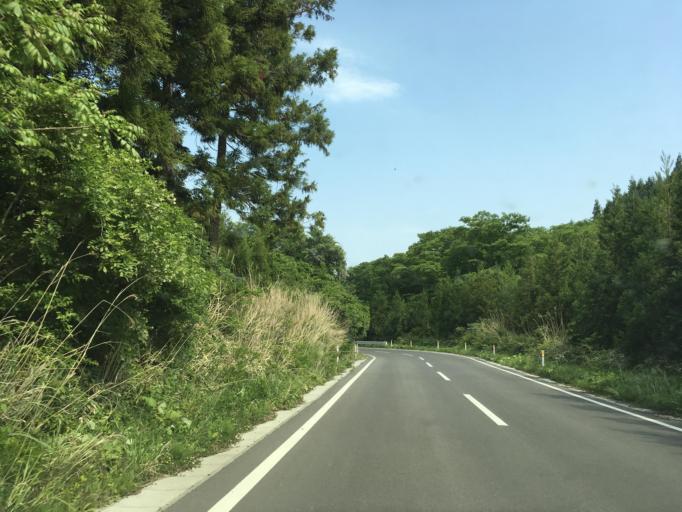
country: JP
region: Iwate
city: Ofunato
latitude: 38.8532
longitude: 141.4916
